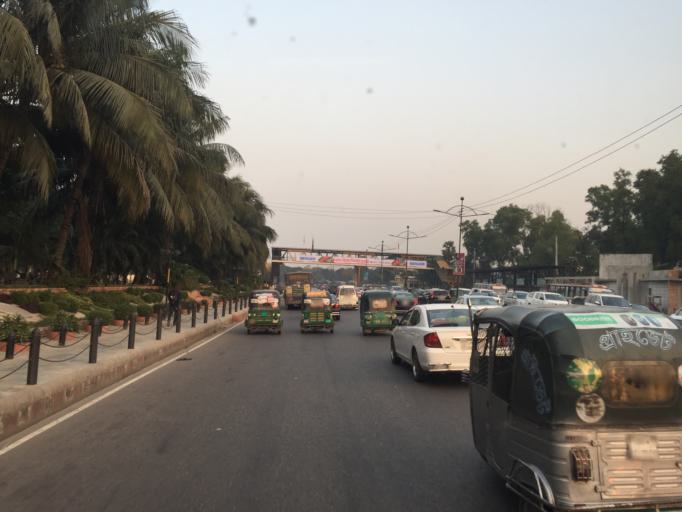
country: BD
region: Dhaka
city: Tungi
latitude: 23.8170
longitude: 90.4091
